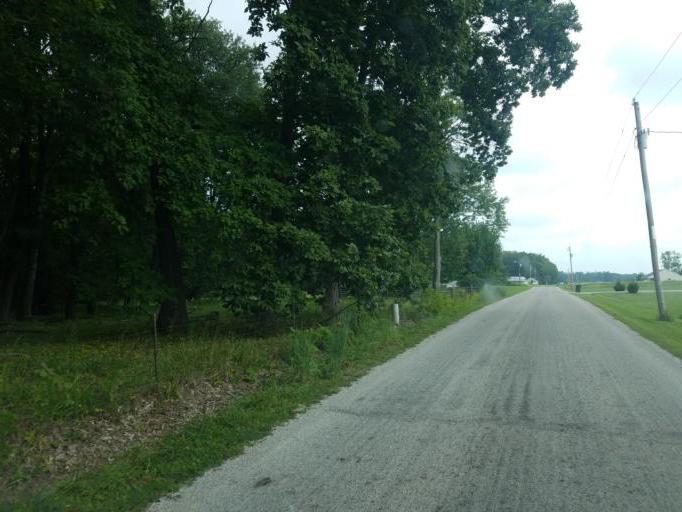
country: US
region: Ohio
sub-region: Morrow County
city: Mount Gilead
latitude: 40.4918
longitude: -82.8107
